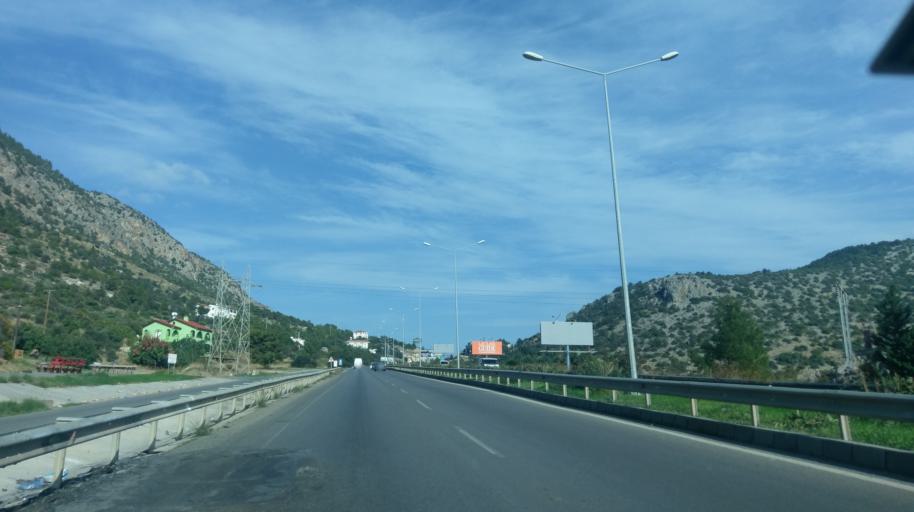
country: CY
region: Keryneia
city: Kyrenia
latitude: 35.2981
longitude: 33.2811
